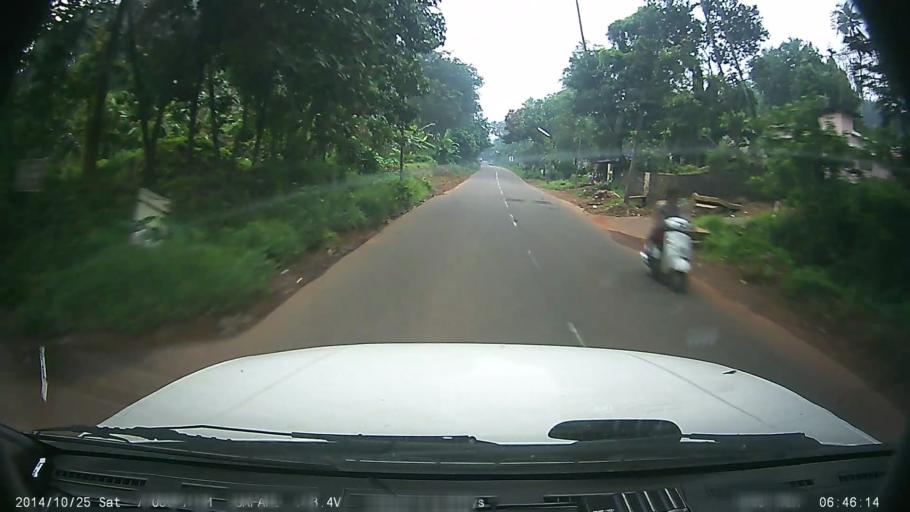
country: IN
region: Kerala
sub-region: Ernakulam
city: Muvattupuzha
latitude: 9.9423
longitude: 76.5756
